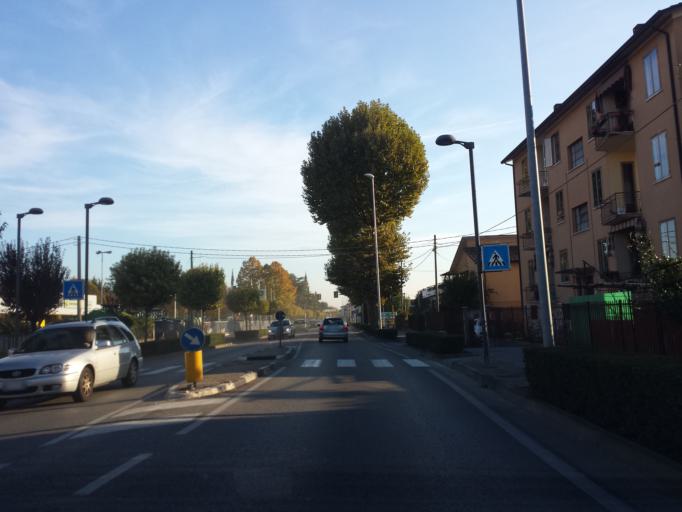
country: IT
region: Veneto
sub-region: Provincia di Vicenza
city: Motta
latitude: 45.6013
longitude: 11.4944
